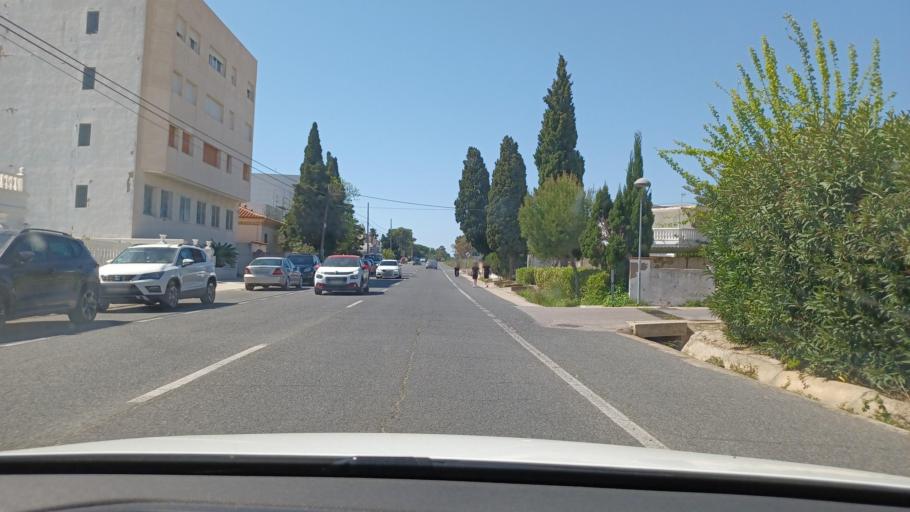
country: ES
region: Catalonia
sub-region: Provincia de Tarragona
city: Sant Carles de la Rapita
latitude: 40.6048
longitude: 0.5807
